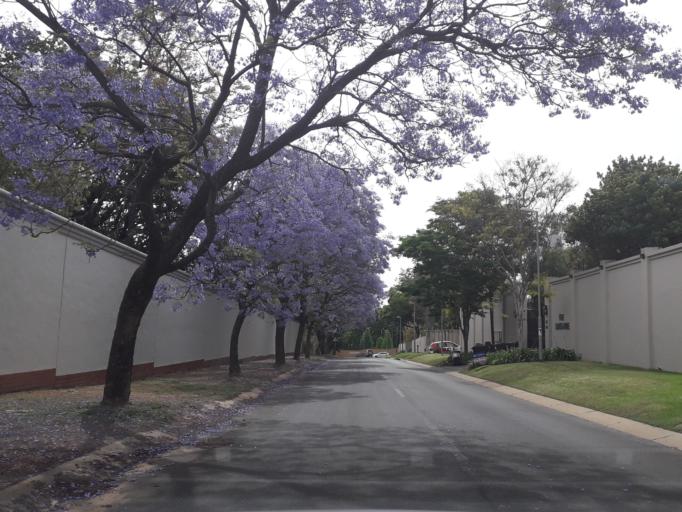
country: ZA
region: Gauteng
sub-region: City of Johannesburg Metropolitan Municipality
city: Diepsloot
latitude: -26.0598
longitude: 28.0152
